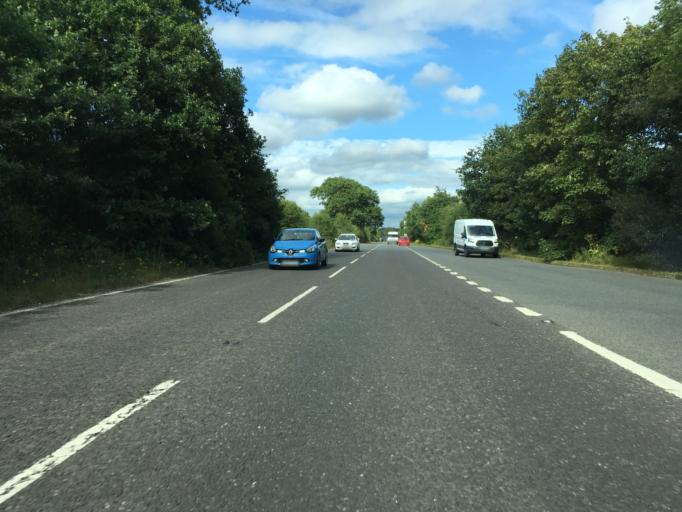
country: GB
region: England
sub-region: West Sussex
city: Horsham
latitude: 51.0723
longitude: -0.3482
